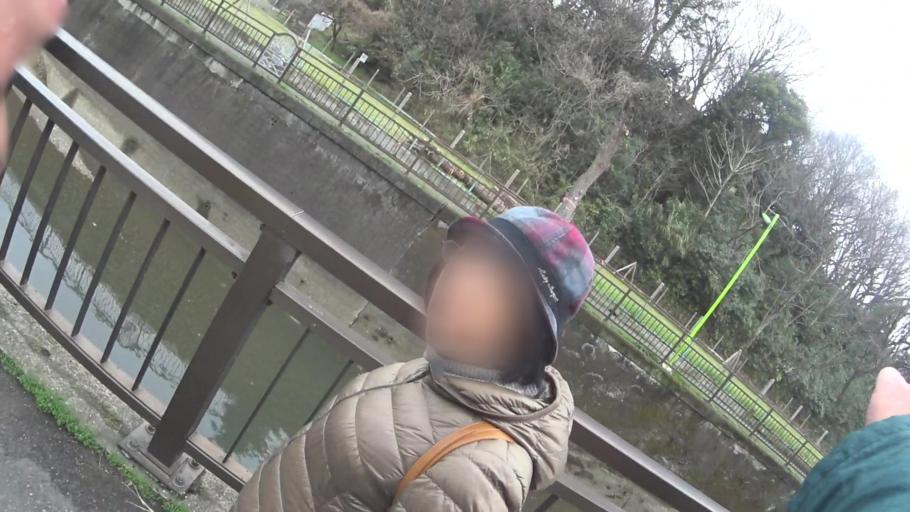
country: JP
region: Tokyo
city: Chofugaoka
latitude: 35.6307
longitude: 139.6090
